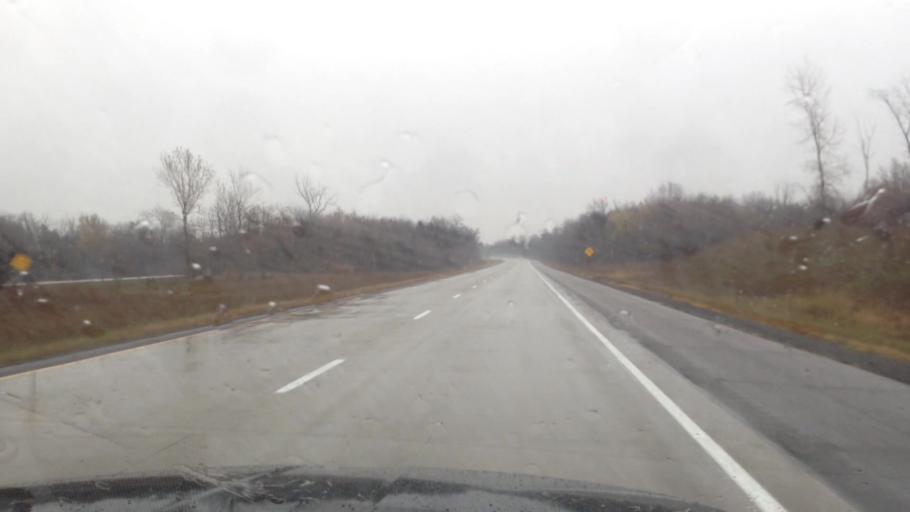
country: CA
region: Ontario
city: Casselman
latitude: 45.3802
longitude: -74.8201
